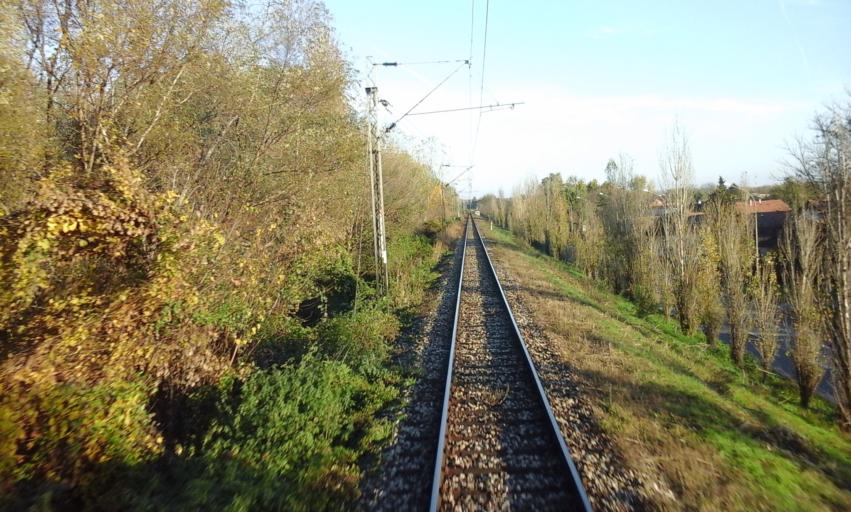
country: RS
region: Autonomna Pokrajina Vojvodina
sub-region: Juznobacki Okrug
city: Petrovaradin
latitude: 45.2580
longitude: 19.8698
